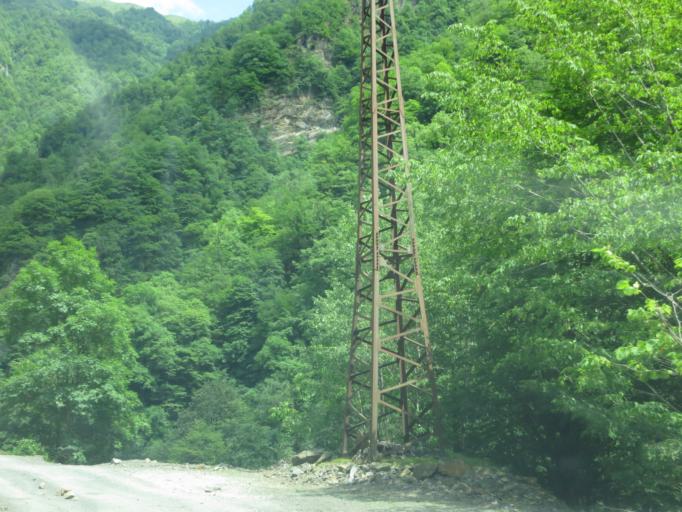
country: GE
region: Kakheti
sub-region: Telavi
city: Telavi
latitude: 42.2041
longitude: 45.4663
